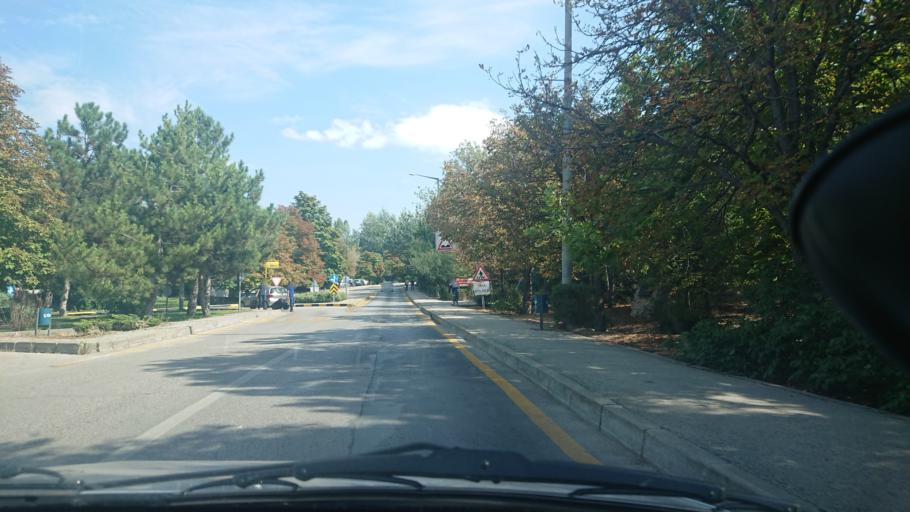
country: TR
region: Ankara
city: Ankara
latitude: 39.8916
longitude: 32.7887
